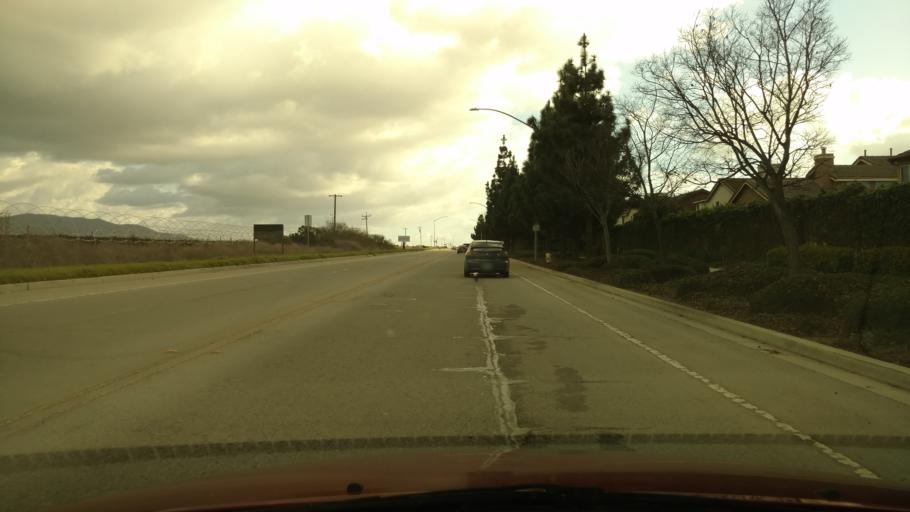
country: US
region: California
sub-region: Monterey County
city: Salinas
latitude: 36.6989
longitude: -121.5991
